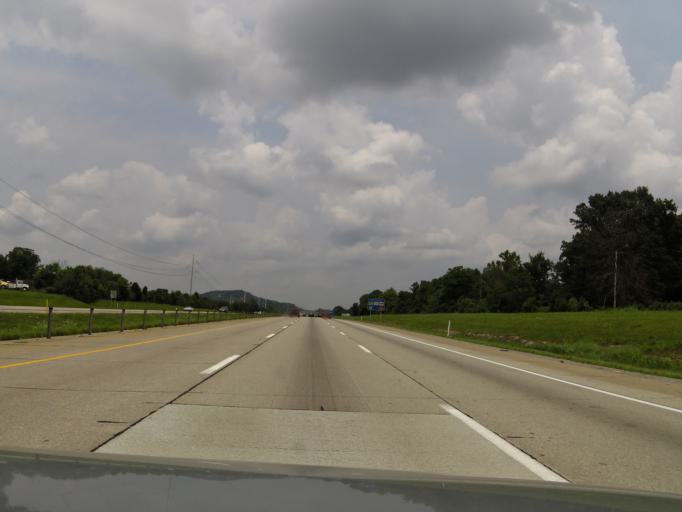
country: US
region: Kentucky
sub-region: Bullitt County
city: Brooks
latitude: 38.0529
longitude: -85.6983
